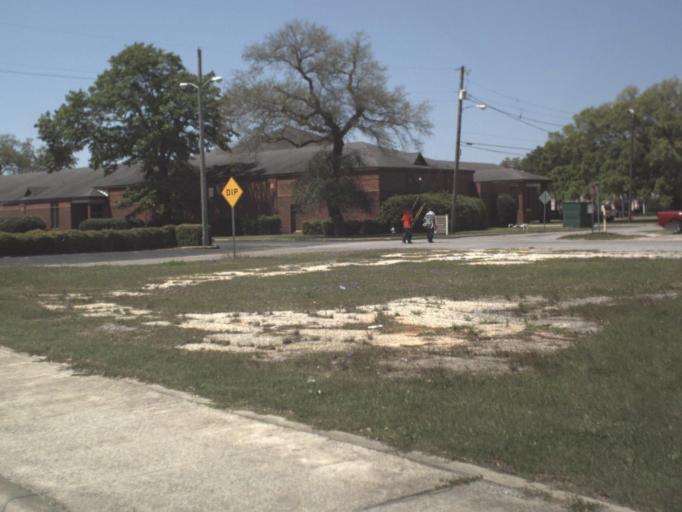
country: US
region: Florida
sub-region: Escambia County
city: West Pensacola
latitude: 30.4218
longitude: -87.2521
